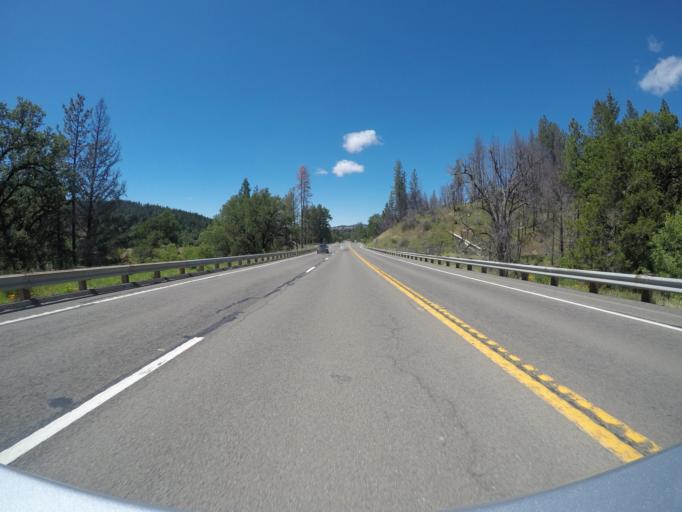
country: US
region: California
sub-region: Mendocino County
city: Laytonville
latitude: 39.7188
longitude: -123.5006
